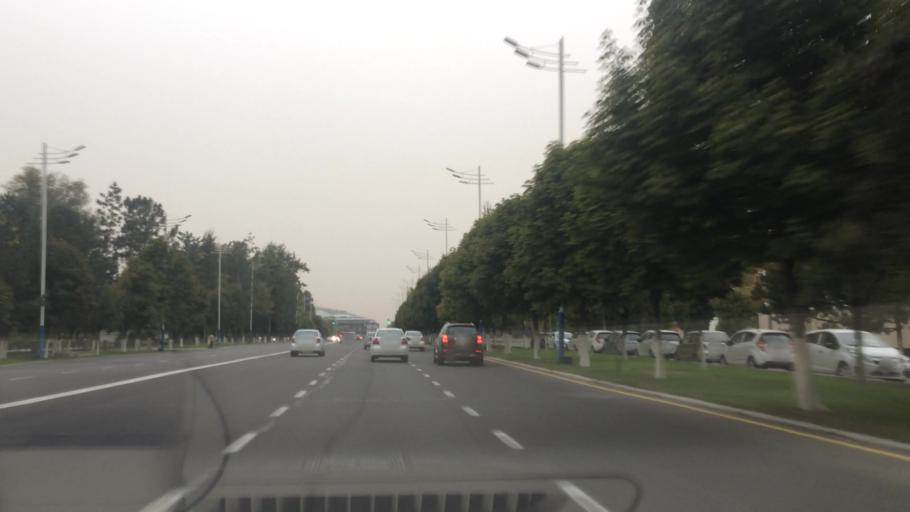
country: UZ
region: Toshkent Shahri
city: Tashkent
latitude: 41.3061
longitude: 69.2620
